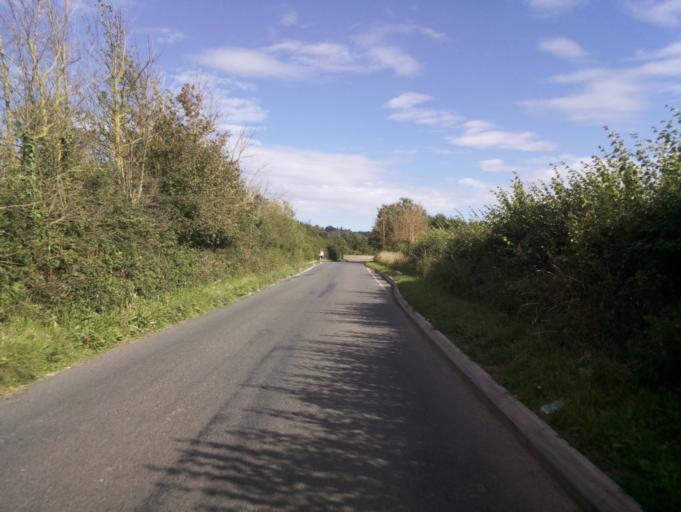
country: GB
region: England
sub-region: Gloucestershire
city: Gloucester
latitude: 51.8082
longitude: -2.2530
